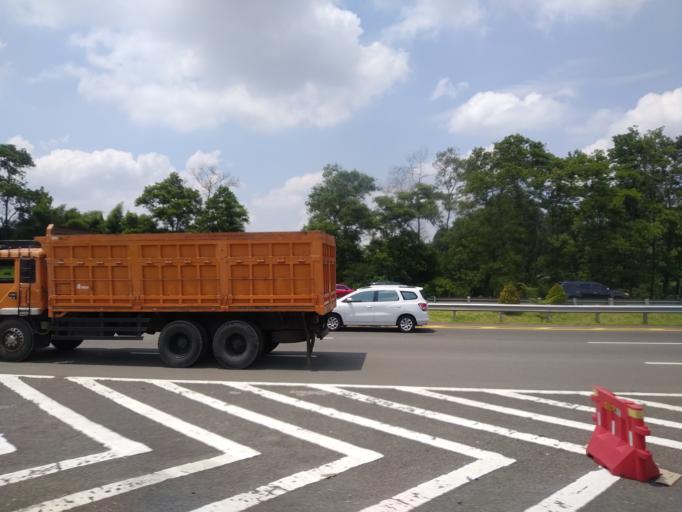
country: ID
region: West Java
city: Bogor
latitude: -6.5925
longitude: 106.8341
